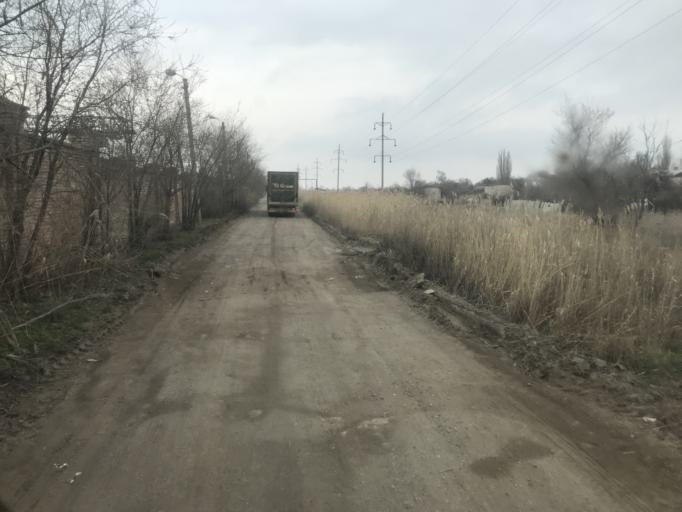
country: RU
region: Volgograd
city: Krasnoslobodsk
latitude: 48.5288
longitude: 44.5903
